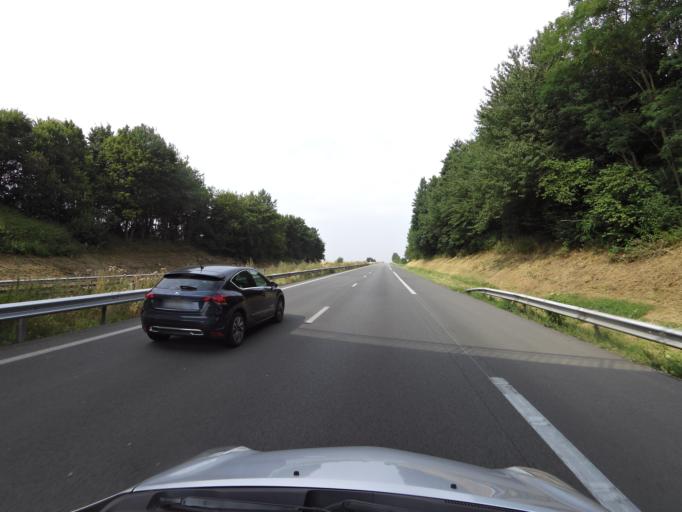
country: FR
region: Picardie
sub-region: Departement de la Somme
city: Epehy
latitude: 50.0325
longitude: 3.1722
